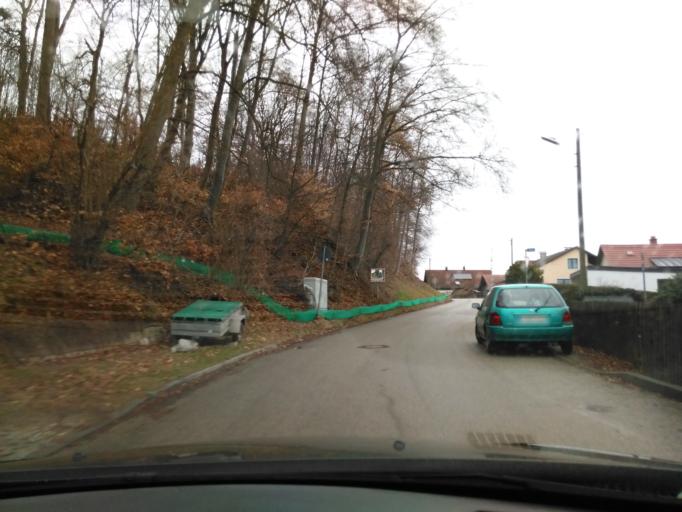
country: DE
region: Bavaria
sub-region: Upper Bavaria
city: Fuerstenfeldbruck
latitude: 48.1844
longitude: 11.2209
